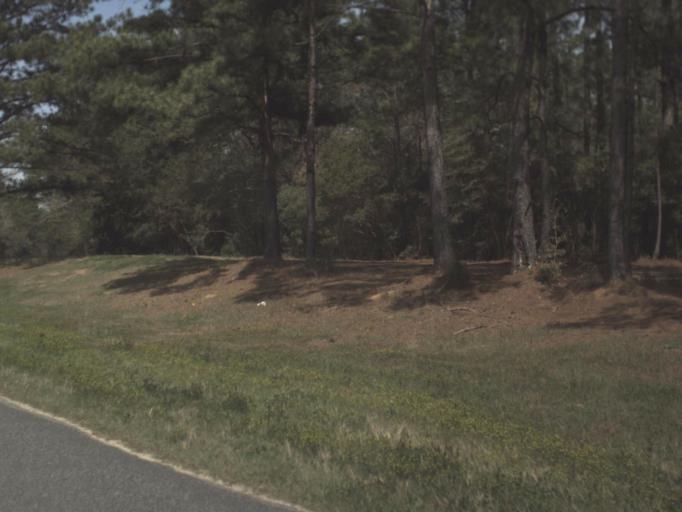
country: US
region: Florida
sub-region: Walton County
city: DeFuniak Springs
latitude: 30.7262
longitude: -85.9646
